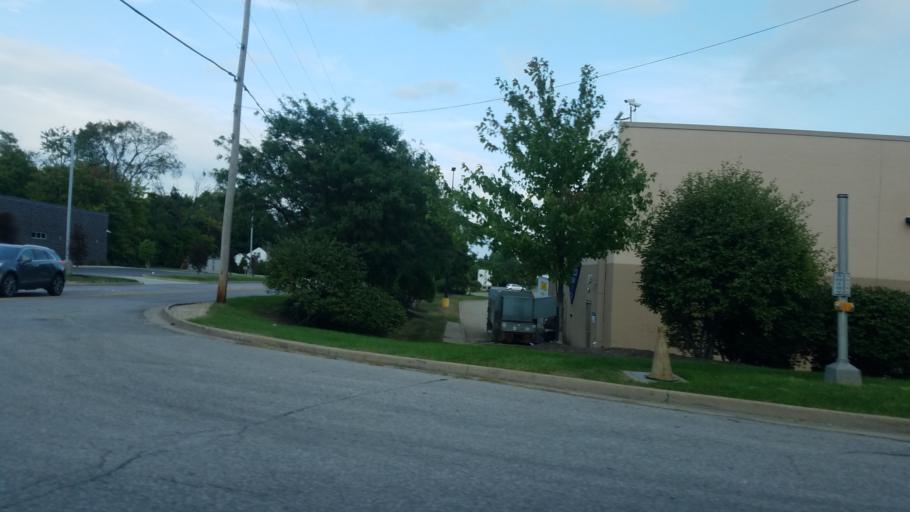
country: US
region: Ohio
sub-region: Mahoning County
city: Poland
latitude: 41.0349
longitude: -80.6346
